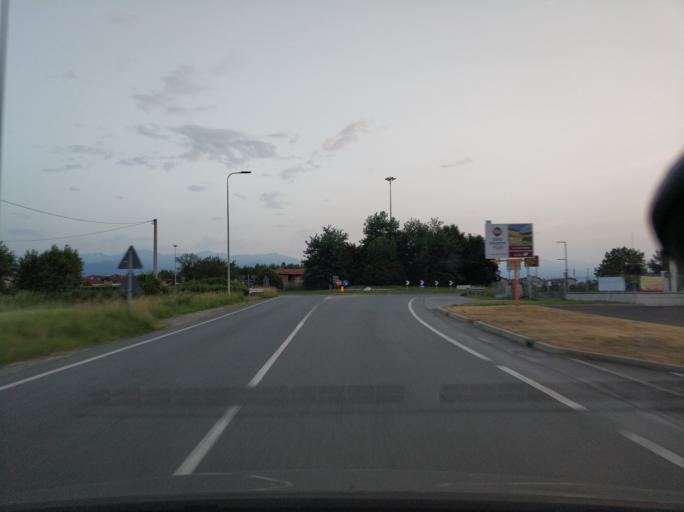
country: IT
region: Piedmont
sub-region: Provincia di Torino
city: San Maurizio
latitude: 45.2044
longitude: 7.6366
